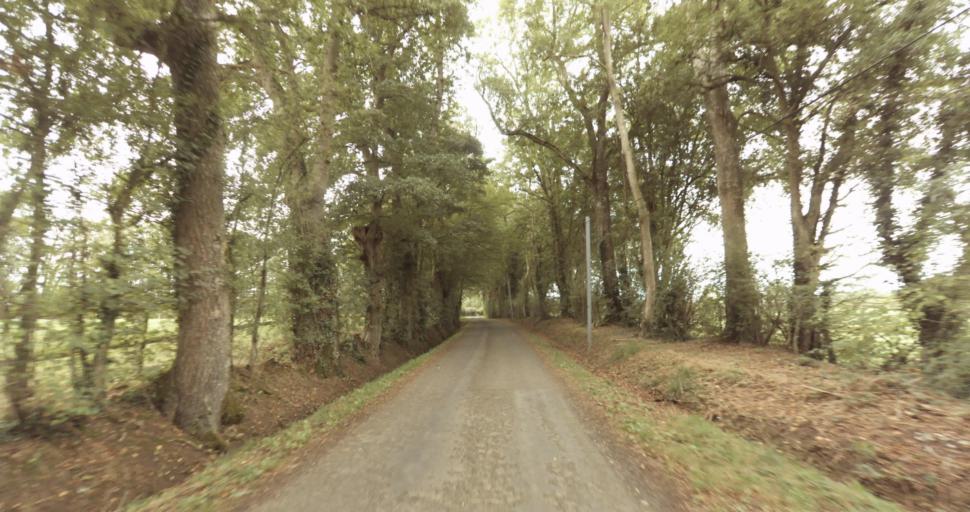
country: FR
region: Lower Normandy
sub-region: Departement de l'Orne
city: Gace
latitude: 48.7464
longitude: 0.2940
